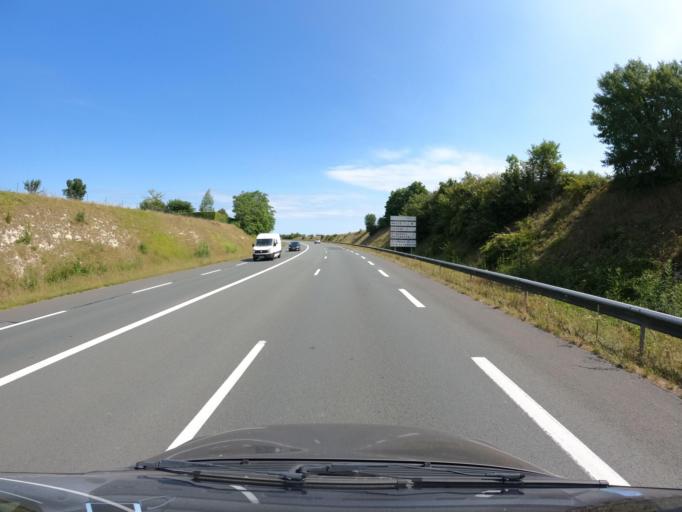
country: FR
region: Poitou-Charentes
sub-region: Departement des Deux-Sevres
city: Mauze-sur-le-Mignon
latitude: 46.1925
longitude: -0.6624
